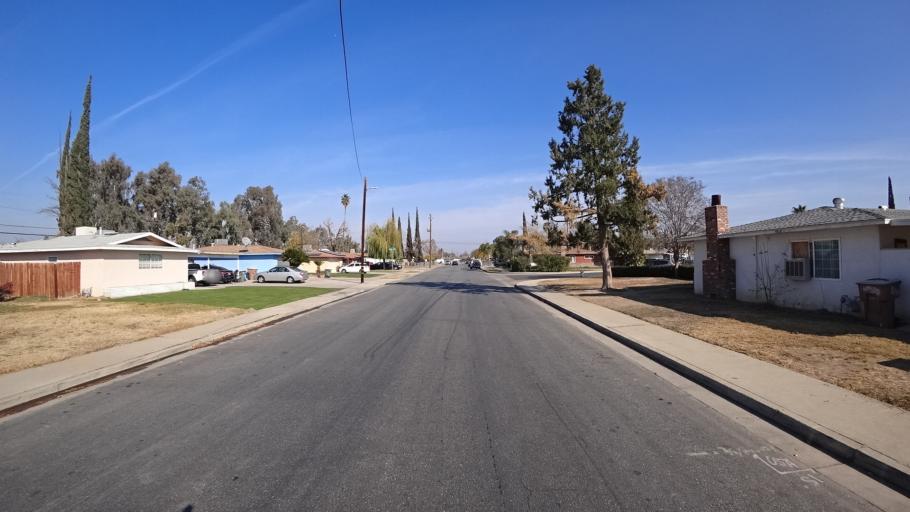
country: US
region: California
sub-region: Kern County
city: Bakersfield
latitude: 35.3223
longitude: -119.0197
